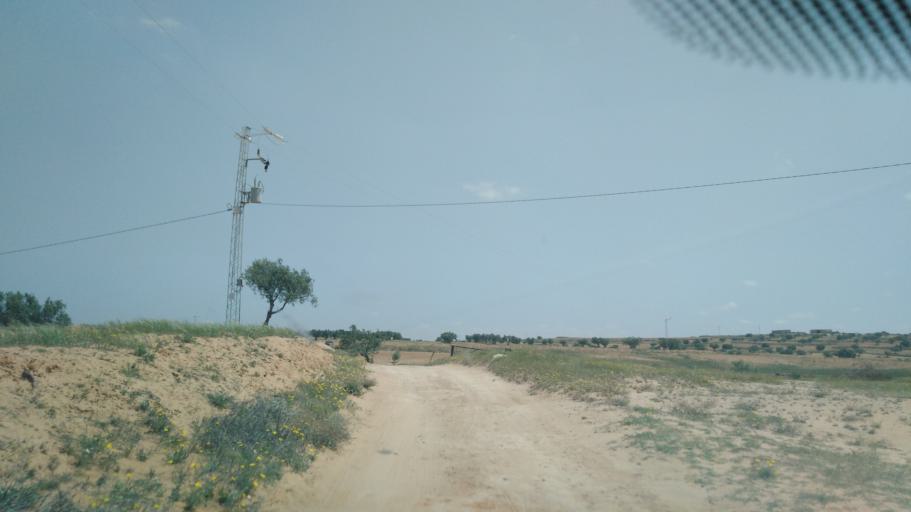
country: TN
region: Safaqis
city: Sfax
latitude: 34.7681
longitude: 10.5699
